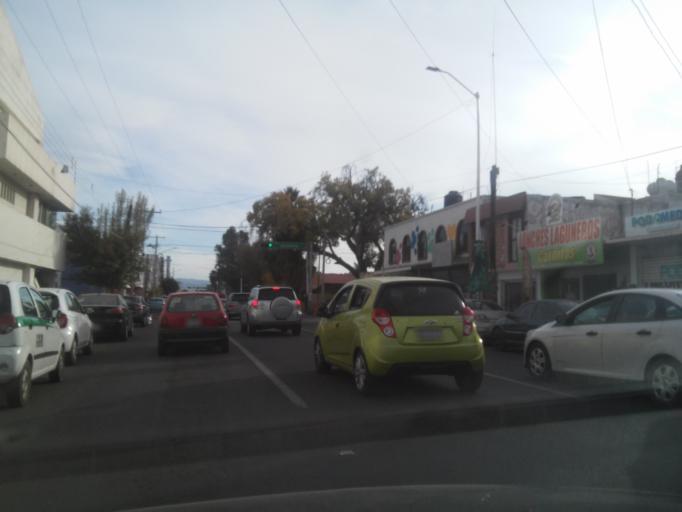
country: MX
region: Durango
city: Victoria de Durango
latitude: 24.0291
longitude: -104.6564
